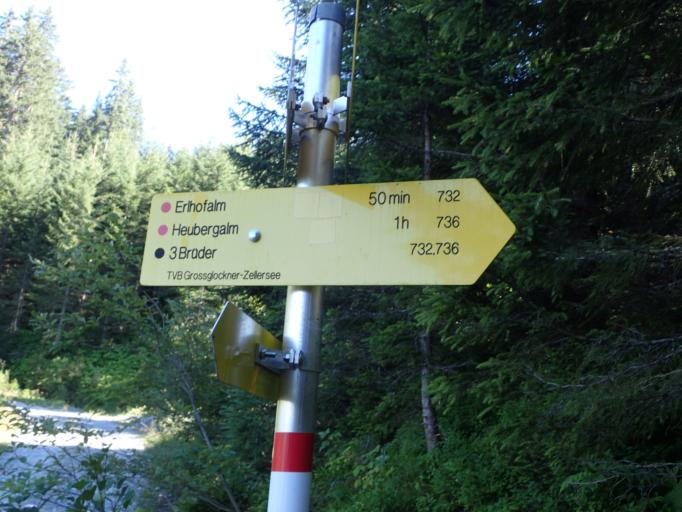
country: AT
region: Salzburg
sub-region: Politischer Bezirk Zell am See
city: Bruck an der Grossglocknerstrasse
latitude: 47.2632
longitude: 12.8756
